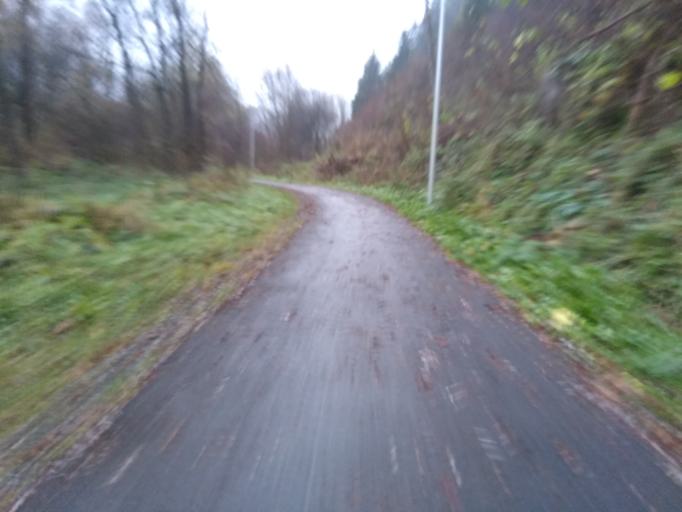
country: AT
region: Styria
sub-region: Politischer Bezirk Bruck-Muerzzuschlag
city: Kapfenberg
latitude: 47.4451
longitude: 15.3112
